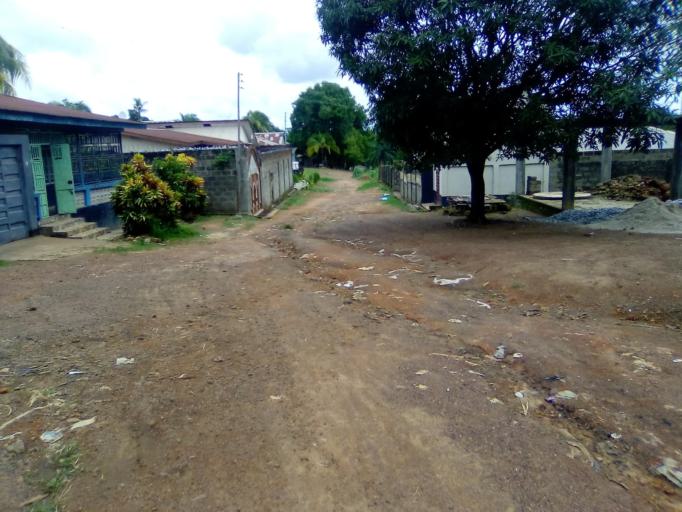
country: SL
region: Southern Province
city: Bo
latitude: 7.9448
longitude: -11.7209
